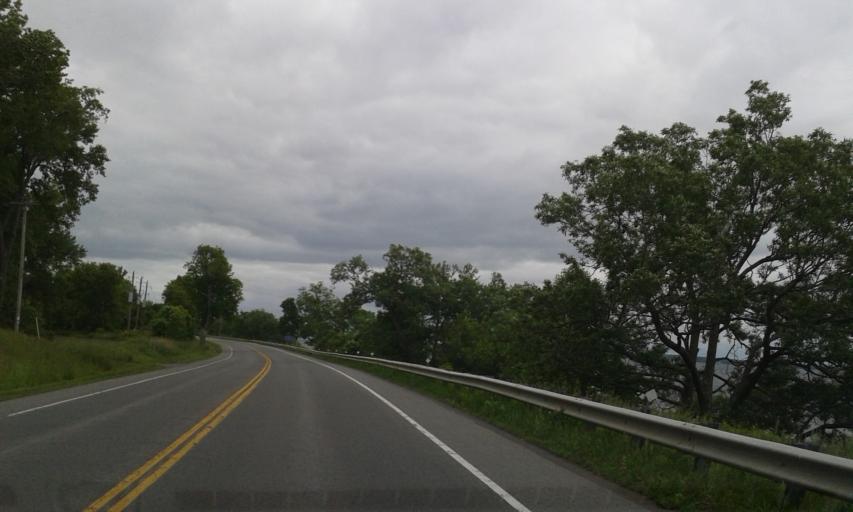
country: CA
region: Ontario
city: Skatepark
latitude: 44.1286
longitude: -76.8732
